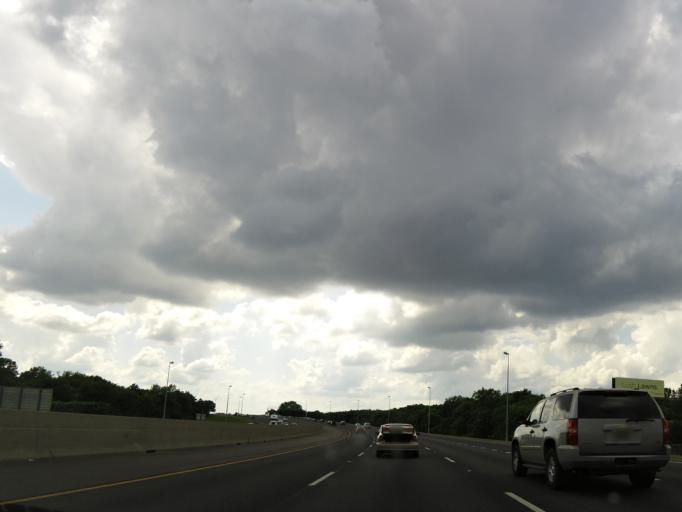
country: US
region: Alabama
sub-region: Jefferson County
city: Tarrant
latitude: 33.5497
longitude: -86.7689
